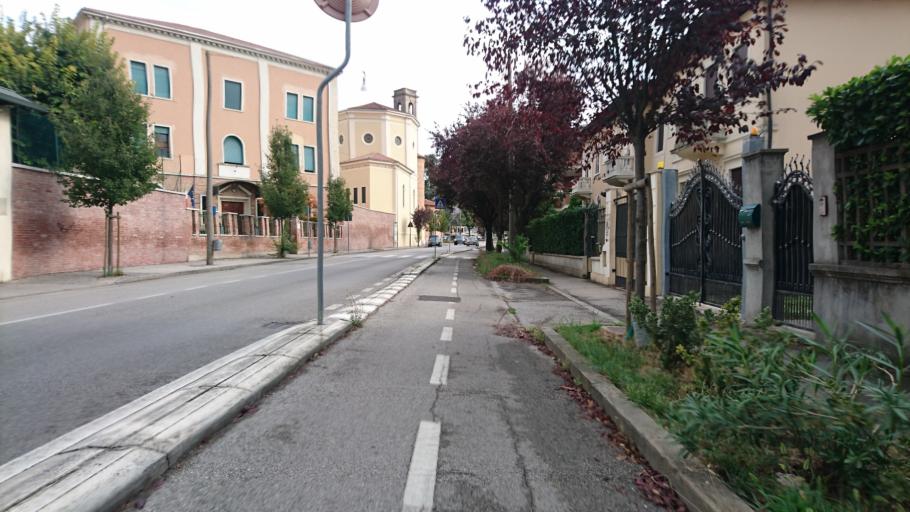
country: IT
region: Veneto
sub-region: Provincia di Padova
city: Padova
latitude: 45.3939
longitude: 11.8702
